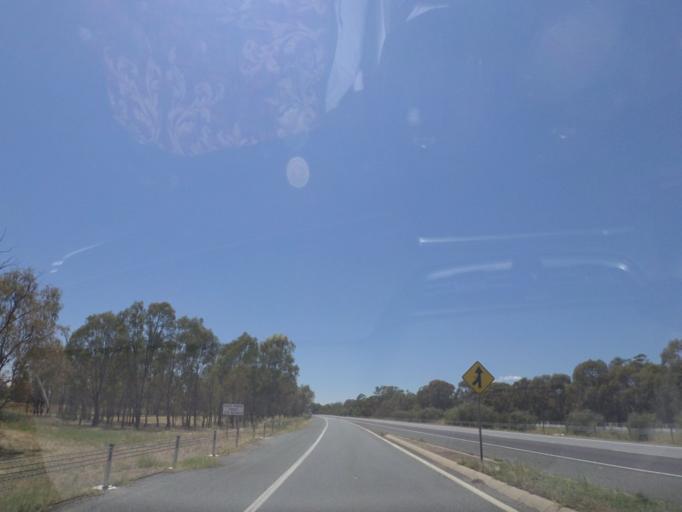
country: AU
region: Victoria
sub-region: Benalla
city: Benalla
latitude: -36.7132
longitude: 145.6380
